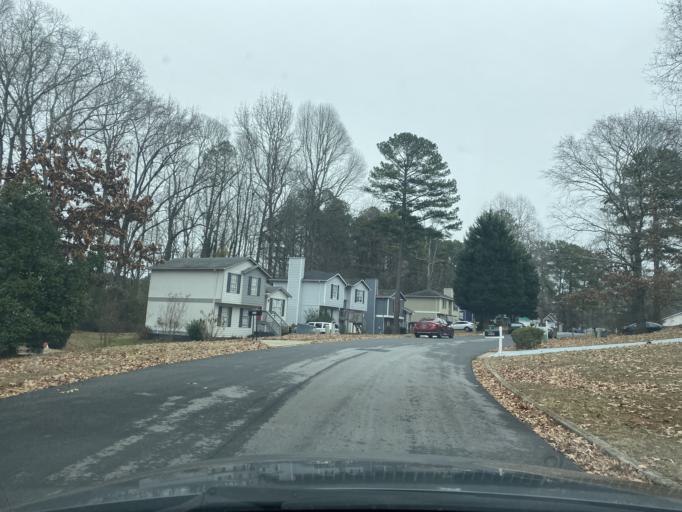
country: US
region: Georgia
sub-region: DeKalb County
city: Pine Mountain
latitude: 33.6974
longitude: -84.1611
